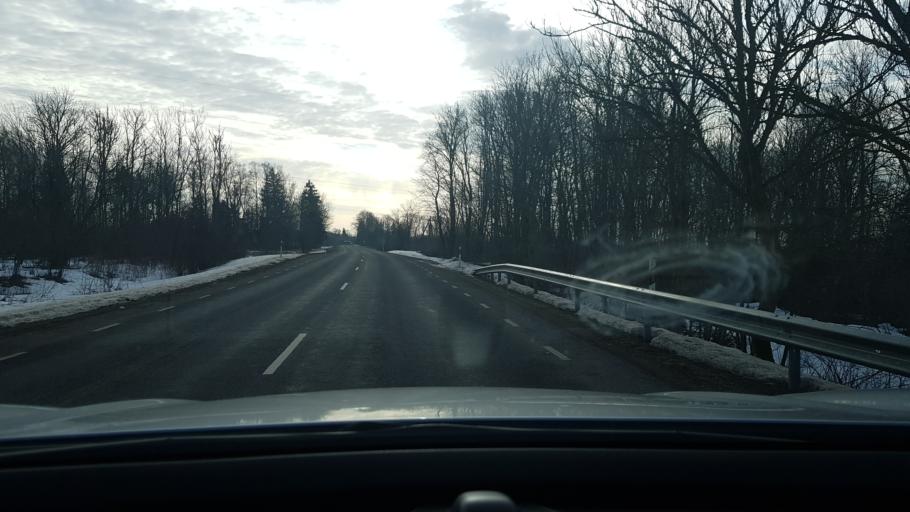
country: EE
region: Saare
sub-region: Kuressaare linn
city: Kuressaare
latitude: 58.2992
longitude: 22.5398
